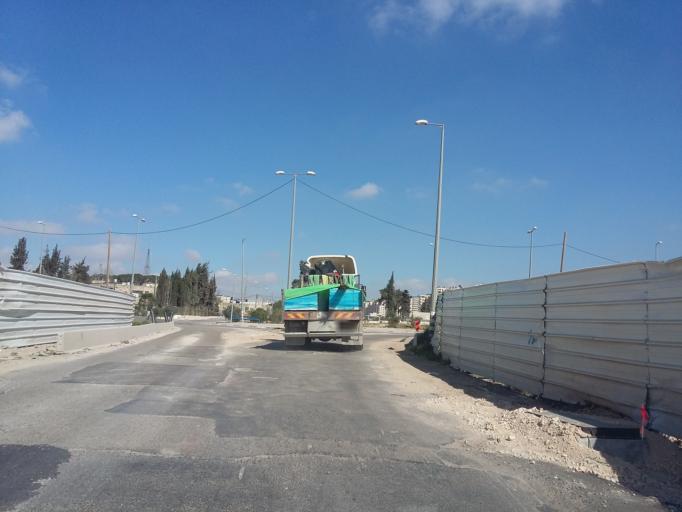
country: PS
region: West Bank
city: Qalandiya
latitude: 31.8603
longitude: 35.2213
